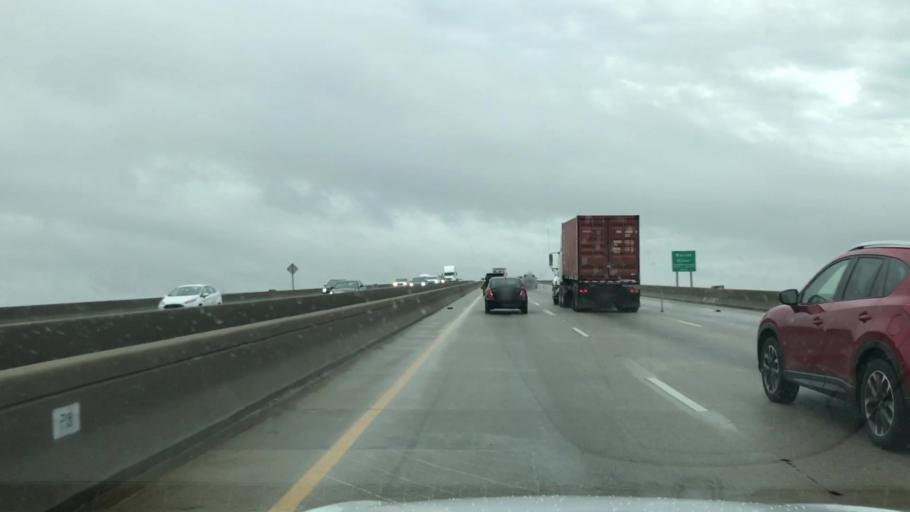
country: US
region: South Carolina
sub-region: Charleston County
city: North Charleston
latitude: 32.8619
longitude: -79.8993
